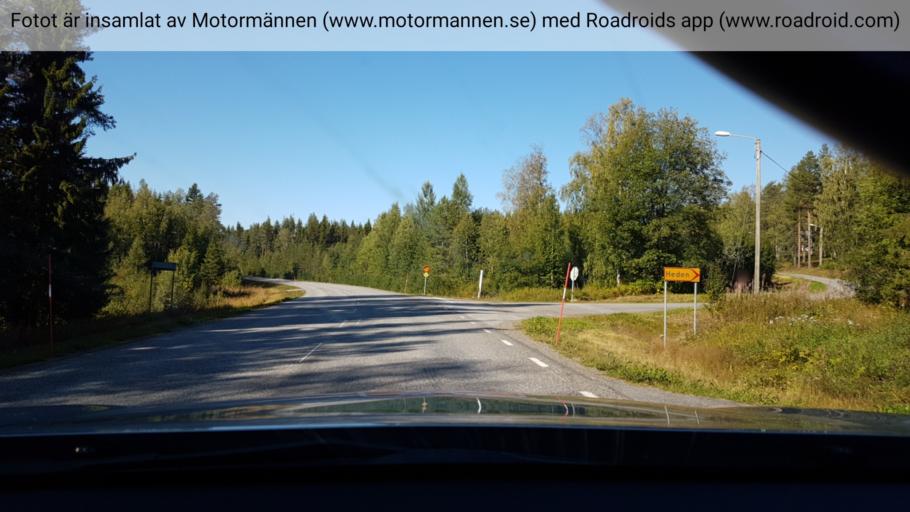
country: SE
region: Vaesterbotten
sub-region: Norsjo Kommun
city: Norsjoe
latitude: 64.9317
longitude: 19.4179
